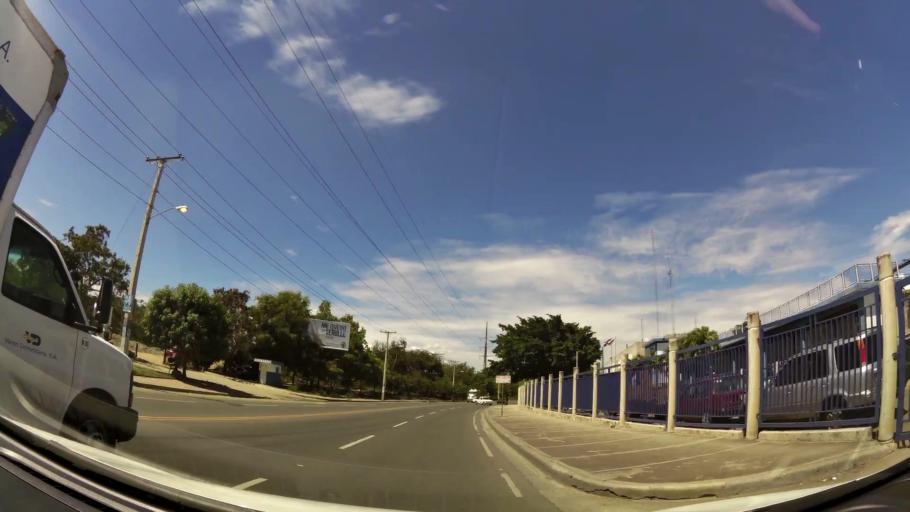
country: DO
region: Santiago
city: Santiago de los Caballeros
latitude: 19.4415
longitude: -70.7031
